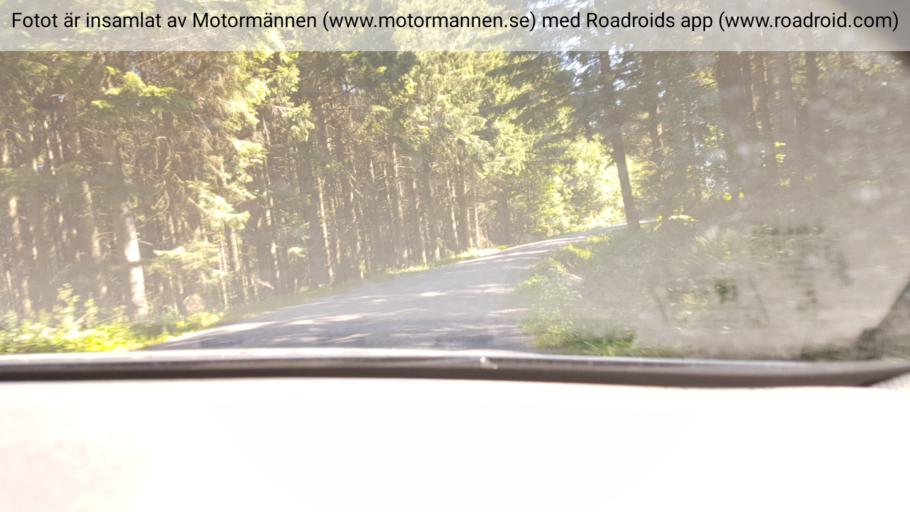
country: SE
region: Vaestra Goetaland
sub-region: Falkopings Kommun
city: Akarp
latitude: 58.1927
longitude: 13.7963
